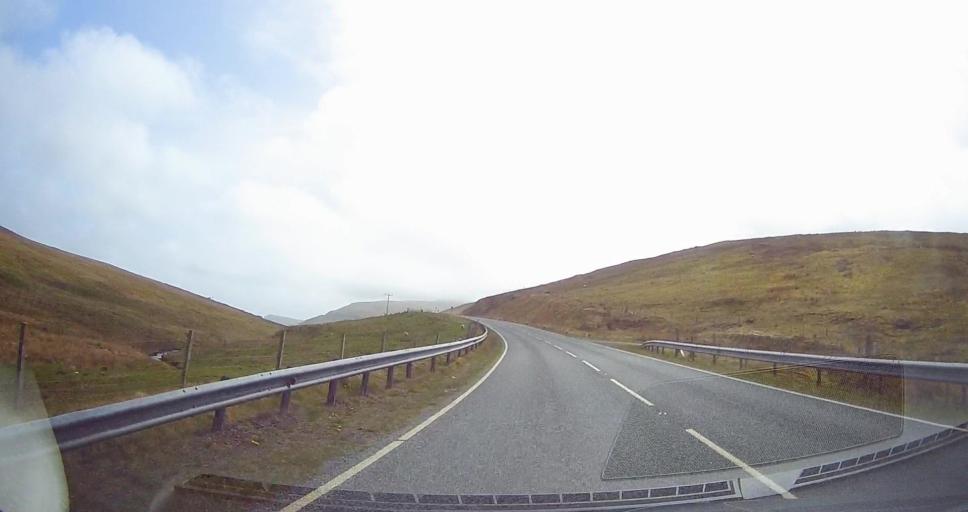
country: GB
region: Scotland
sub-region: Shetland Islands
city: Sandwick
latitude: 60.0039
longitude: -1.2793
